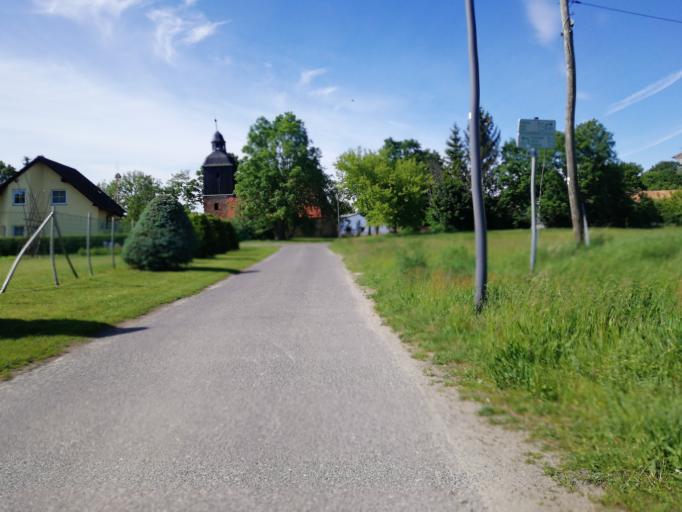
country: DE
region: Brandenburg
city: Calau
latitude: 51.7321
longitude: 13.9121
